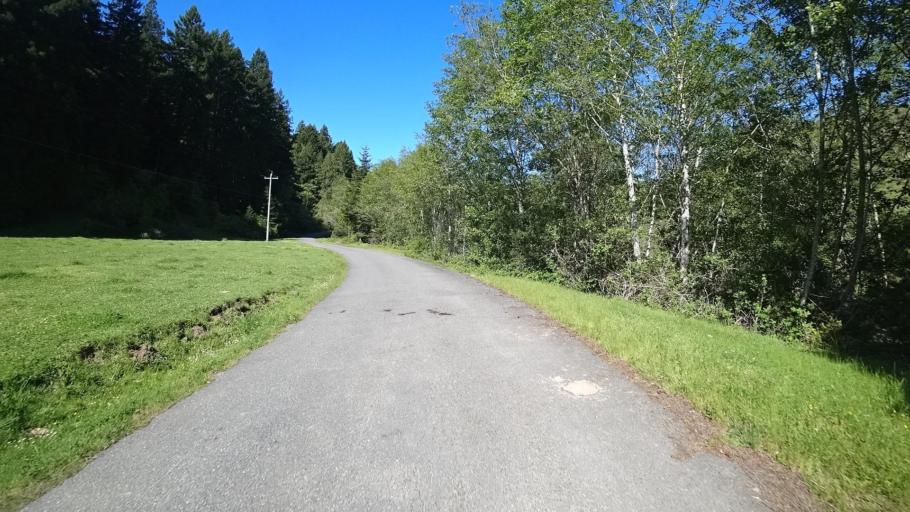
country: US
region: California
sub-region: Humboldt County
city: Fortuna
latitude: 40.5285
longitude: -124.1802
